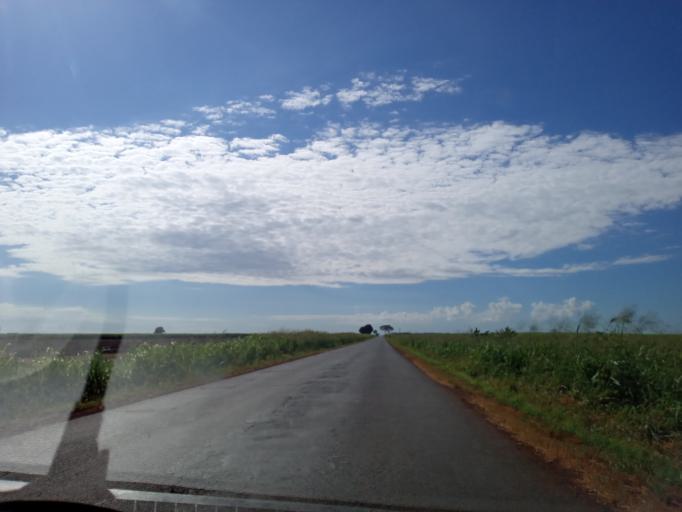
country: BR
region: Goias
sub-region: Itumbiara
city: Itumbiara
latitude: -18.4487
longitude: -49.1653
